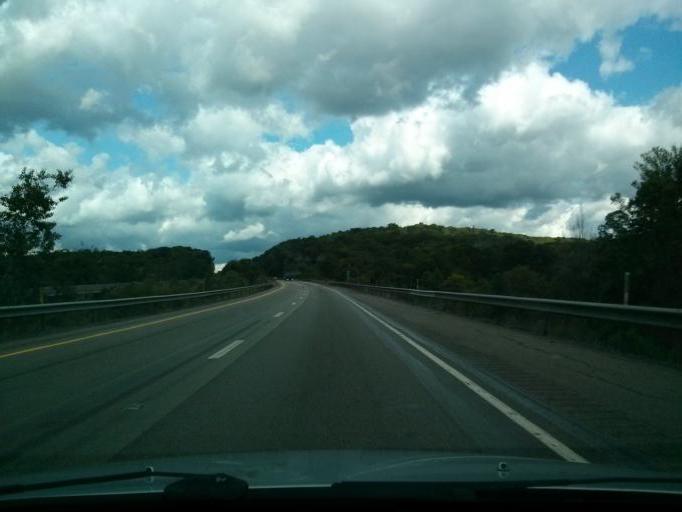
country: US
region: Pennsylvania
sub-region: Jefferson County
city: Brookville
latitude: 41.1597
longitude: -79.0012
